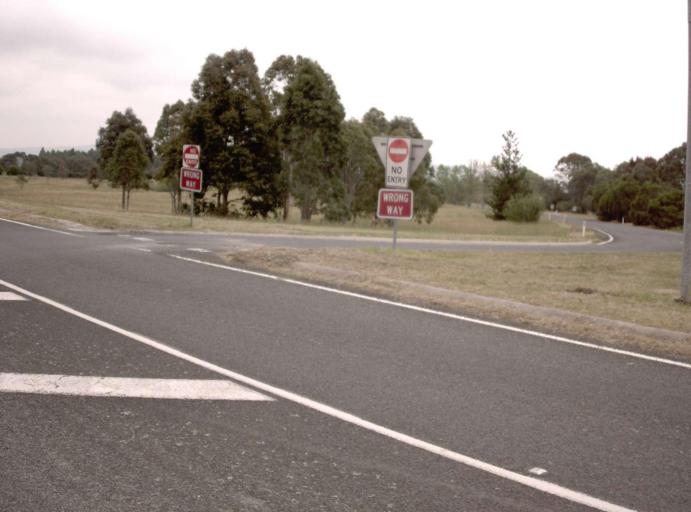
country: AU
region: Victoria
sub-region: Latrobe
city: Morwell
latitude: -38.2331
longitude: 146.3795
